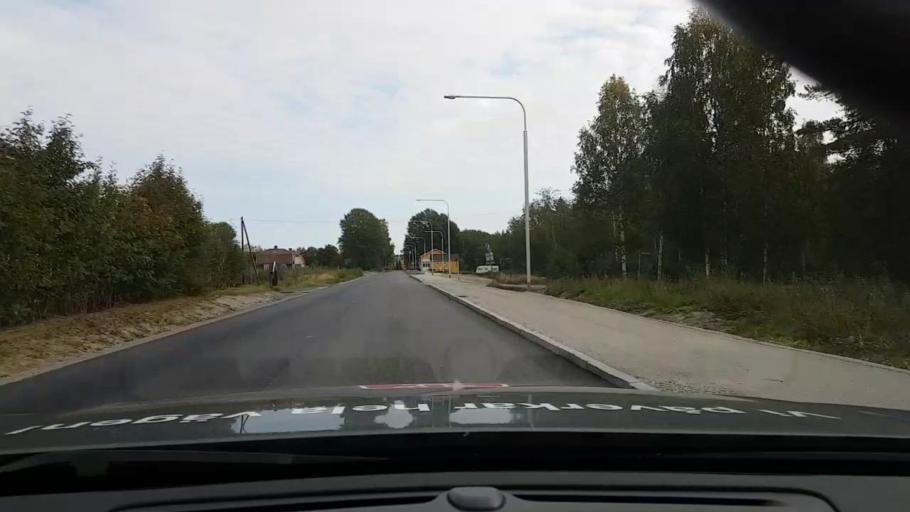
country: SE
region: Vaesternorrland
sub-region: OErnskoeldsviks Kommun
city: Bjasta
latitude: 63.2891
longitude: 18.4443
